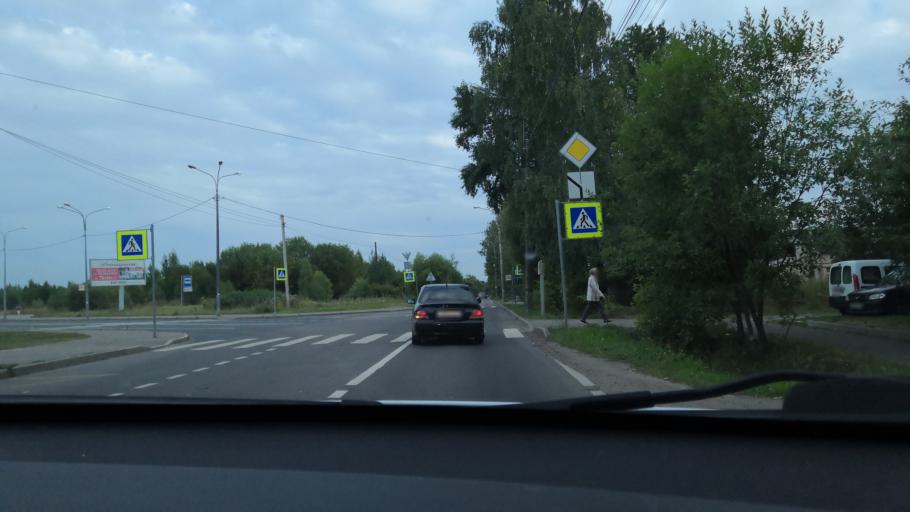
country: RU
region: St.-Petersburg
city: Pushkin
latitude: 59.6958
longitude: 30.4125
